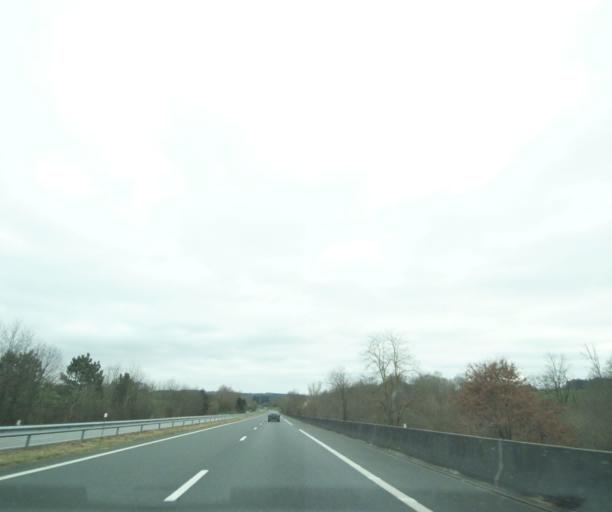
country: FR
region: Limousin
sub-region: Departement de la Correze
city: Vigeois
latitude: 45.4233
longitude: 1.5160
